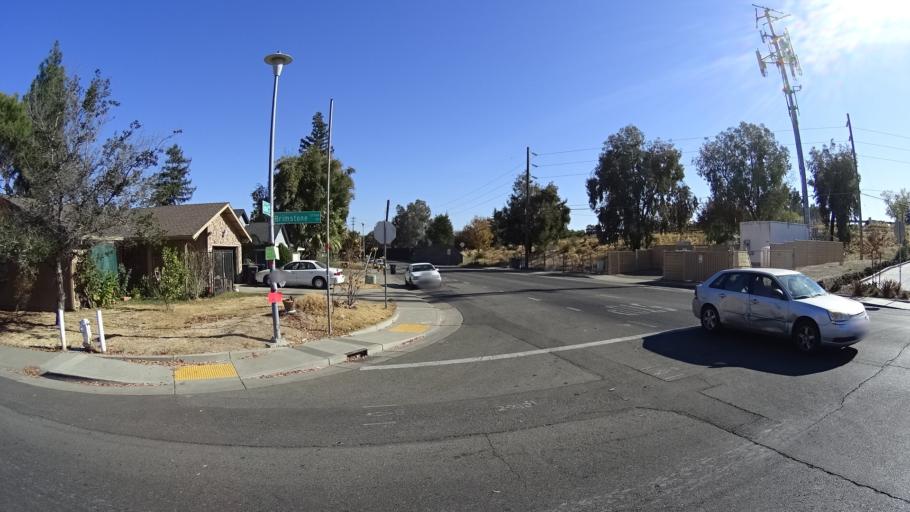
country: US
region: California
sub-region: Sacramento County
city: Antelope
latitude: 38.7087
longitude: -121.3113
